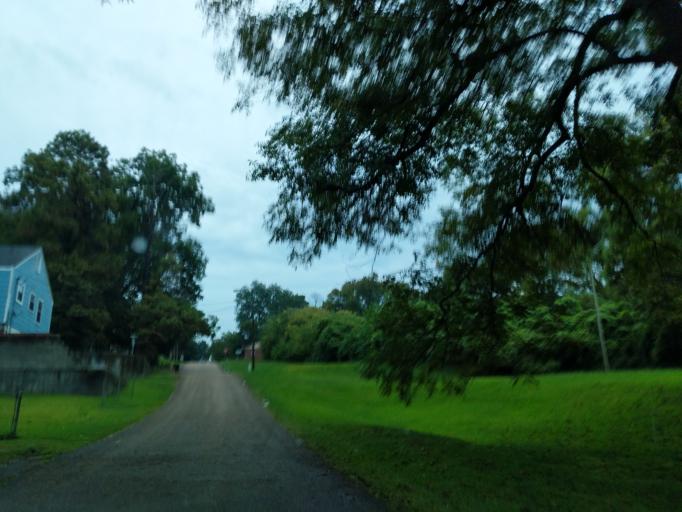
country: US
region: Mississippi
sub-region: Warren County
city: Vicksburg
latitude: 32.3346
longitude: -90.8905
